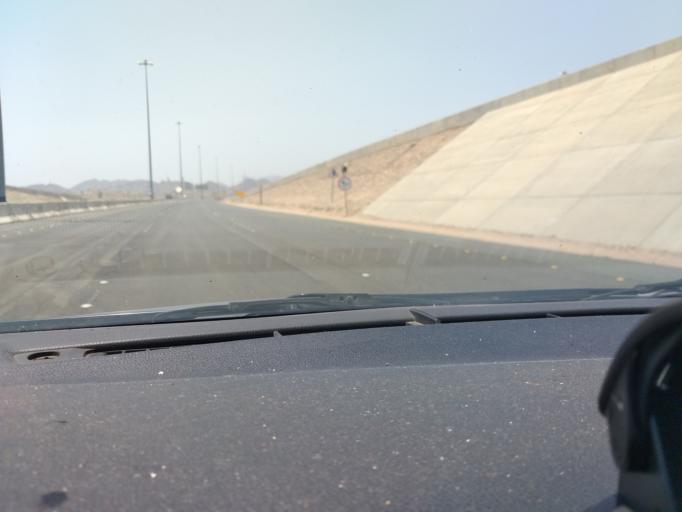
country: SA
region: Makkah
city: Mecca
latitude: 21.3268
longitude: 39.9672
